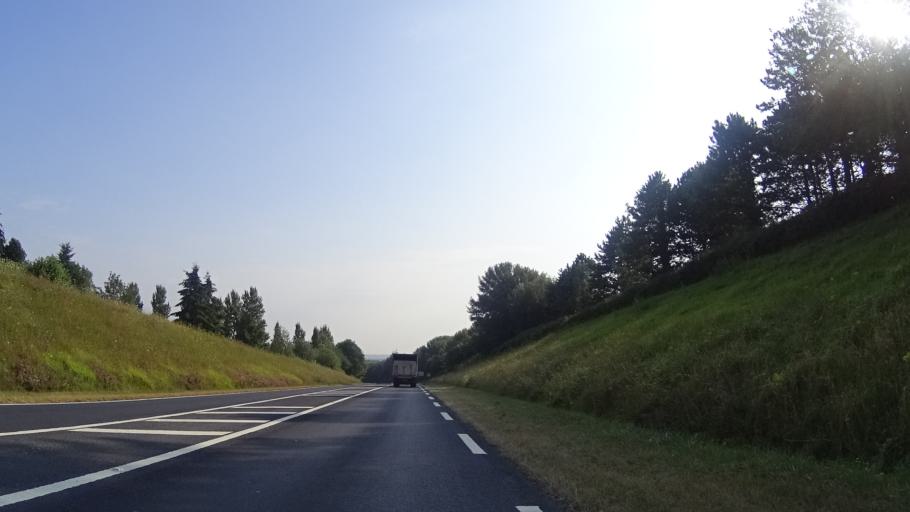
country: FR
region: Ile-de-France
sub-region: Departement du Val-d'Oise
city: Seugy
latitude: 49.1150
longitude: 2.4013
